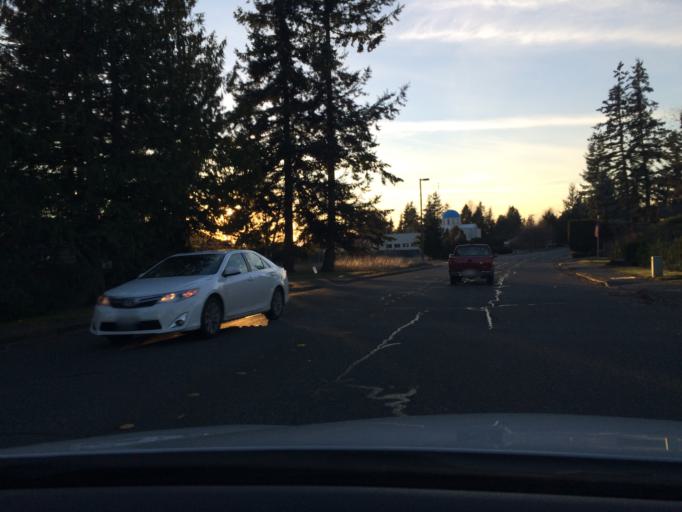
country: US
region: Washington
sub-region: Whatcom County
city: Bellingham
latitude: 48.7699
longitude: -122.4671
